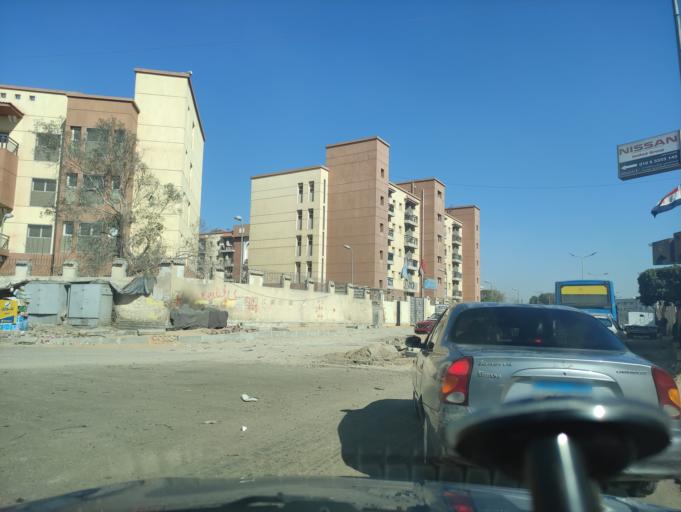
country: EG
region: Muhafazat al Qahirah
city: Cairo
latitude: 30.0559
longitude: 31.2764
